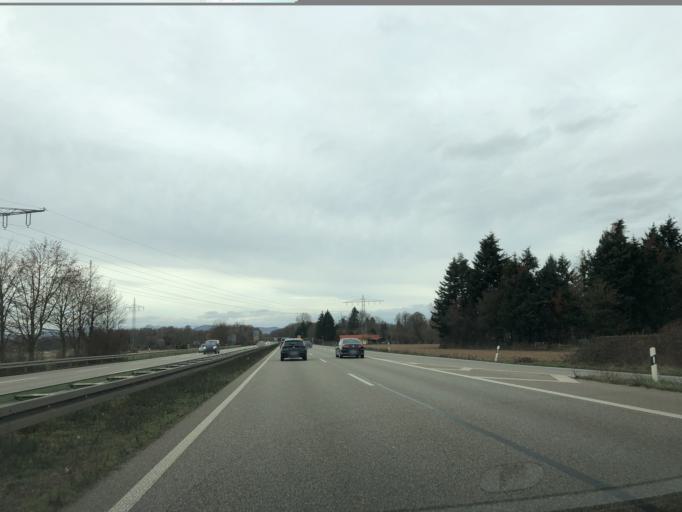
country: DE
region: Baden-Wuerttemberg
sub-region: Freiburg Region
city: Umkirch
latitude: 48.0097
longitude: 7.8004
